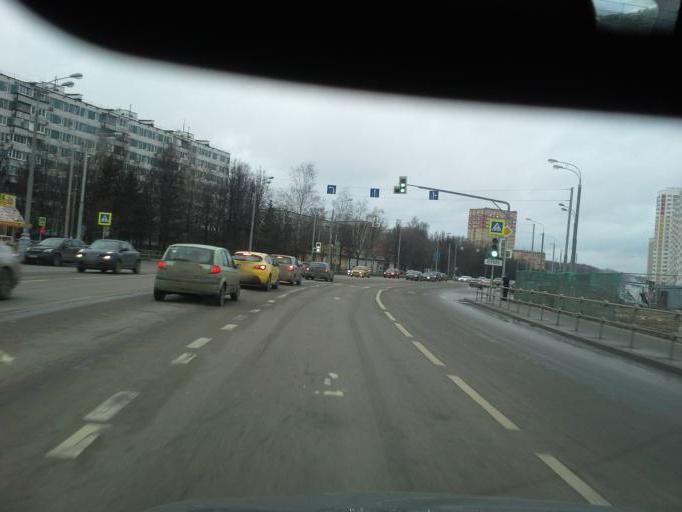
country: RU
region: Moskovskaya
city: Moskovskiy
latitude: 55.5985
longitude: 37.3555
